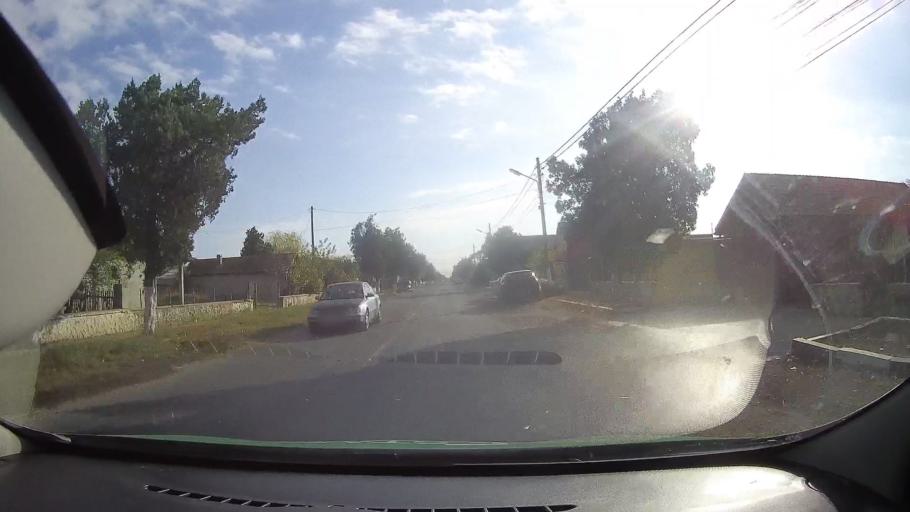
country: RO
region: Constanta
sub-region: Comuna Corbu
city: Corbu
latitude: 44.3920
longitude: 28.6620
